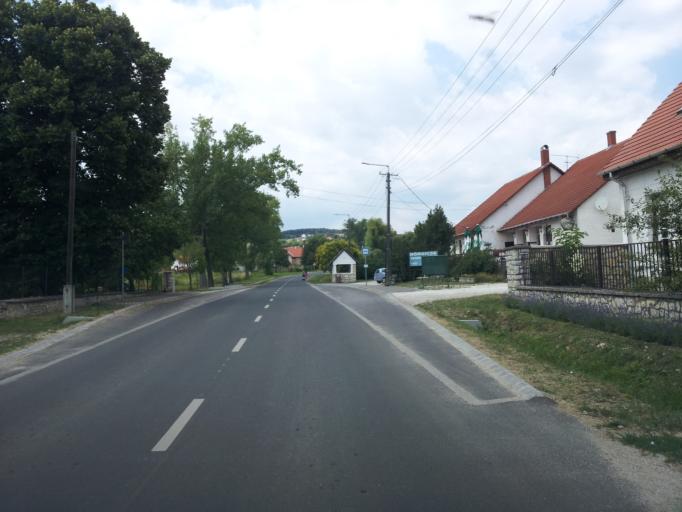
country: HU
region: Veszprem
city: Zanka
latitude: 46.9162
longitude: 17.7224
